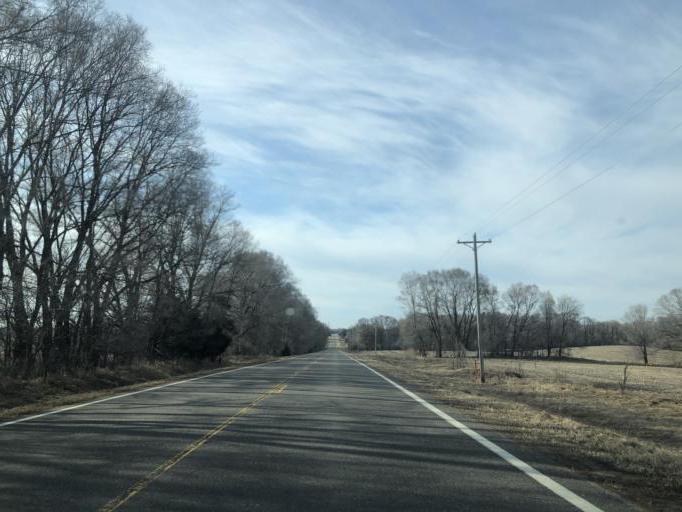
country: US
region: Minnesota
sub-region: Sherburne County
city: Becker
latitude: 45.4150
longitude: -93.8501
